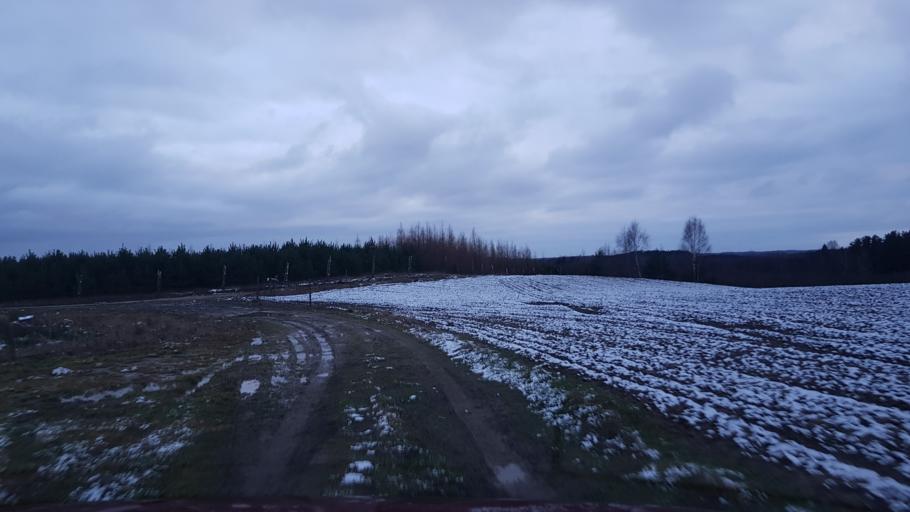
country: PL
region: Pomeranian Voivodeship
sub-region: Powiat bytowski
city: Tuchomie
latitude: 54.1478
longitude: 17.3030
